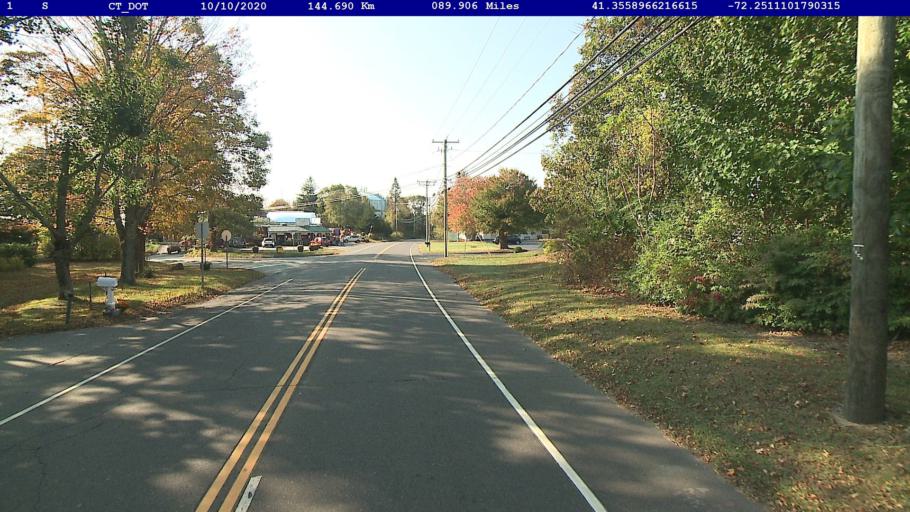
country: US
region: Connecticut
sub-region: New London County
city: Niantic
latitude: 41.3559
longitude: -72.2511
